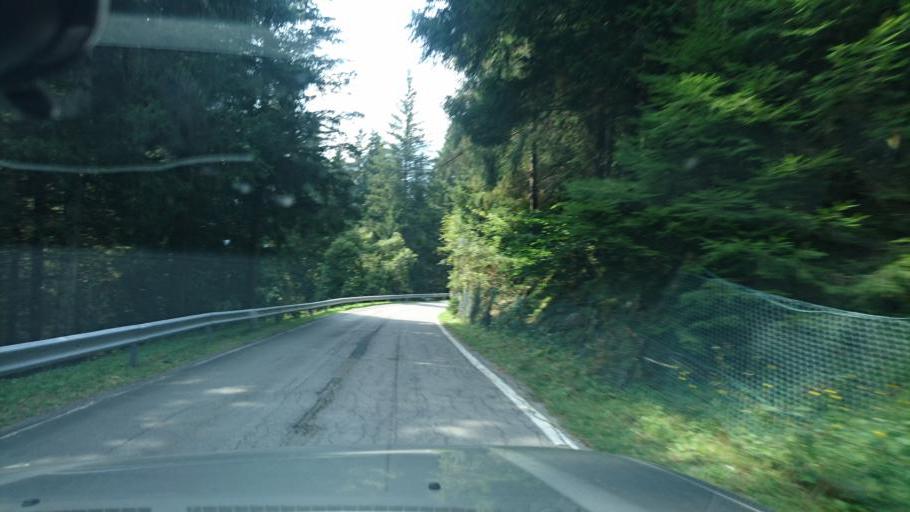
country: IT
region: Lombardy
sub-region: Provincia di Brescia
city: Bagolino
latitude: 45.8959
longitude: 10.4606
